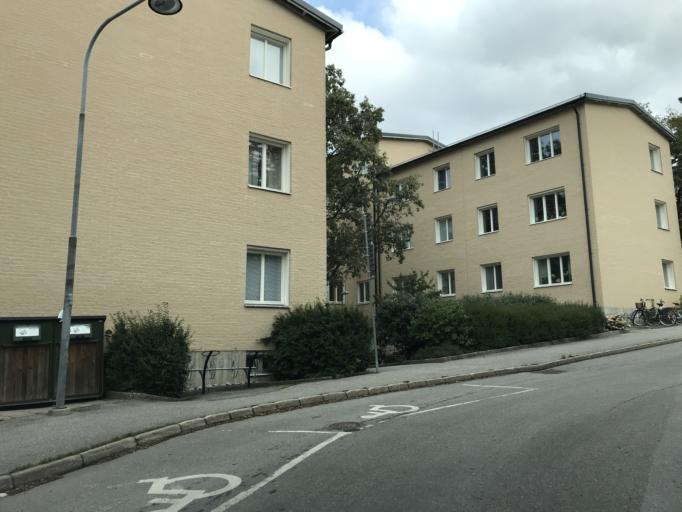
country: SE
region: Stockholm
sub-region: Sundbybergs Kommun
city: Sundbyberg
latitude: 59.3398
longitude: 17.9793
